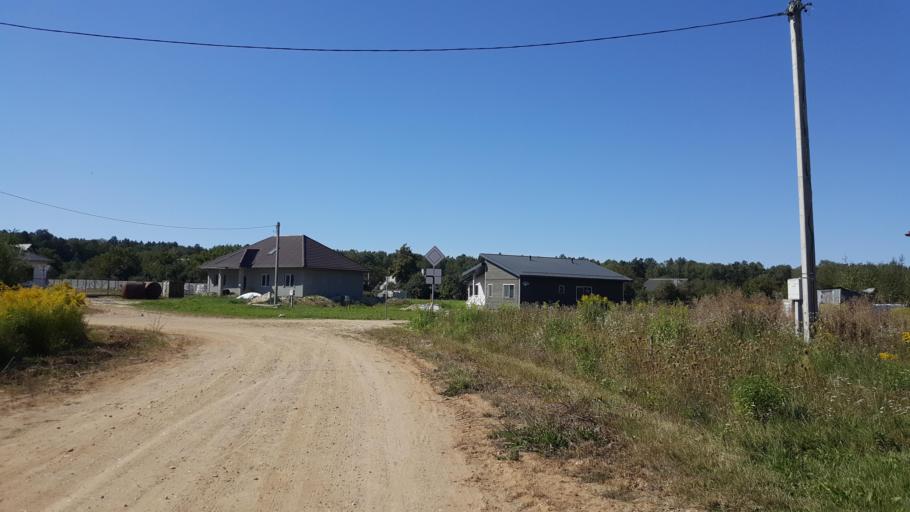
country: BY
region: Brest
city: Vysokaye
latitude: 52.2533
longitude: 23.4973
